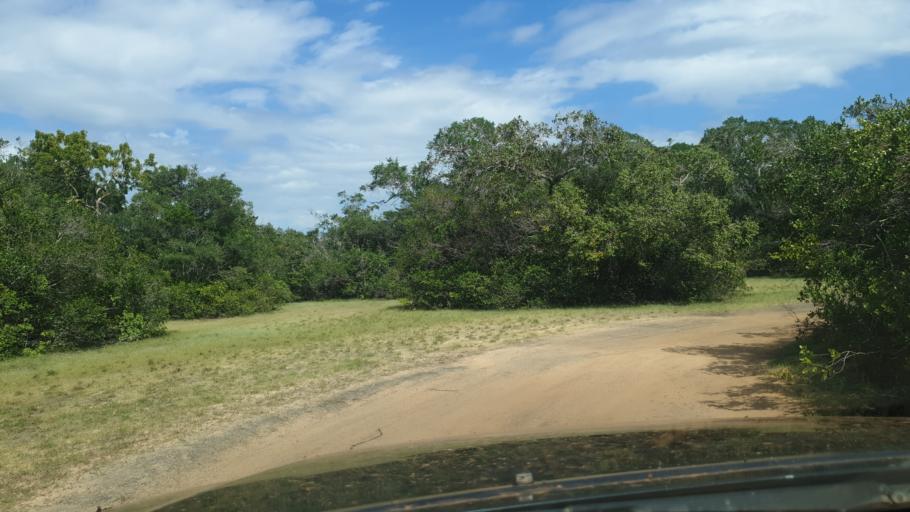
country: LK
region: North Central
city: Anuradhapura
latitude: 8.4267
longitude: 80.0153
